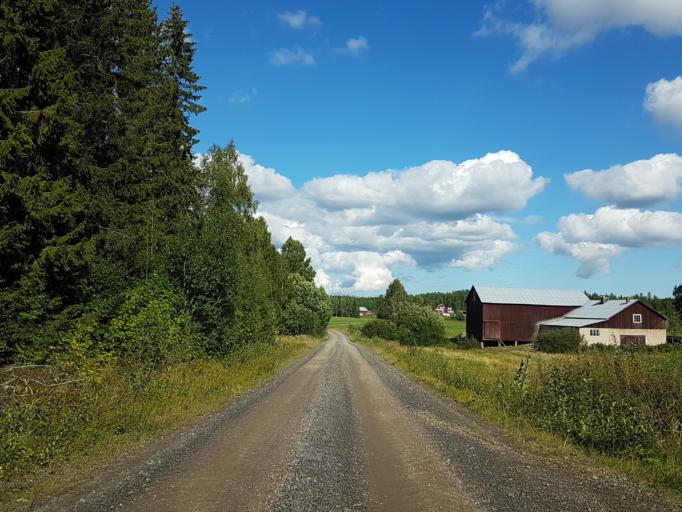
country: SE
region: Vaesterbotten
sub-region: Skelleftea Kommun
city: Burtraesk
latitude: 64.2946
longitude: 20.4719
